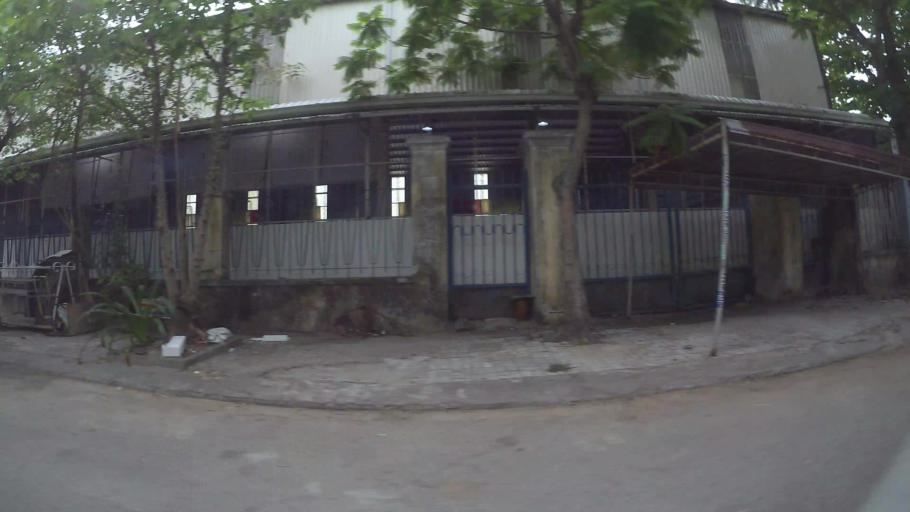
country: VN
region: Da Nang
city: Thanh Khe
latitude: 16.0620
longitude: 108.1836
